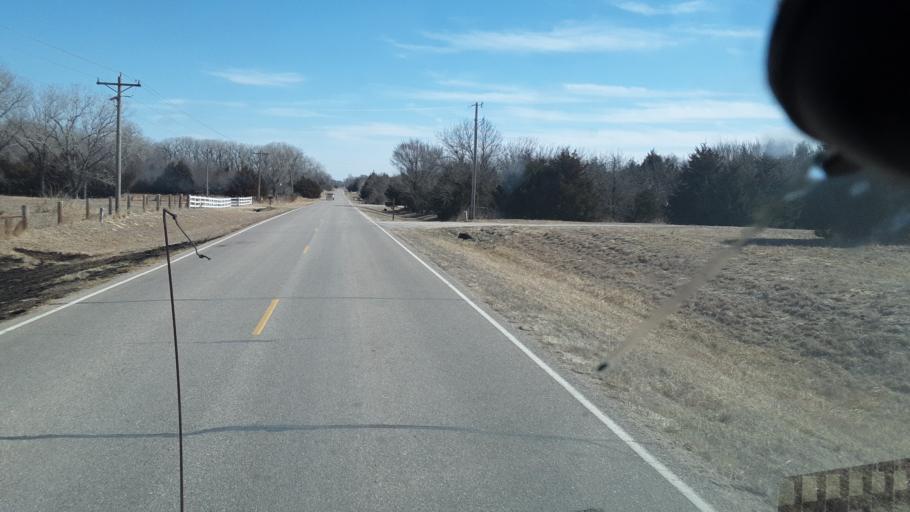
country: US
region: Kansas
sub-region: Reno County
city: Hutchinson
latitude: 38.1592
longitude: -97.9191
